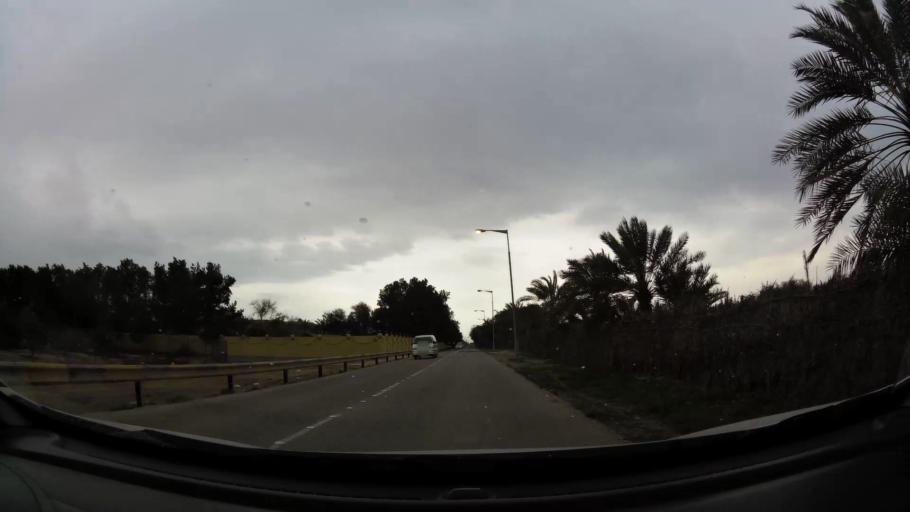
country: BH
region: Central Governorate
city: Madinat Hamad
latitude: 26.1544
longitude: 50.4628
